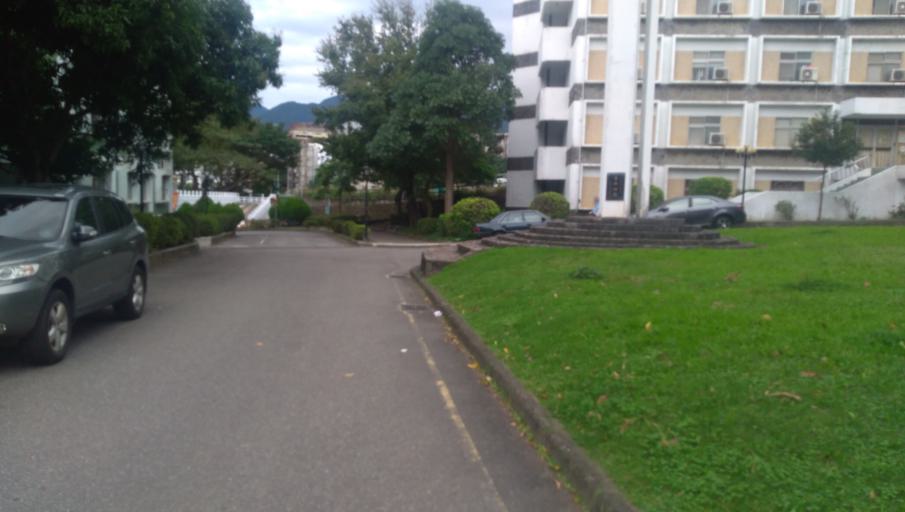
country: TW
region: Taipei
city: Taipei
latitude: 25.1752
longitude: 121.4525
